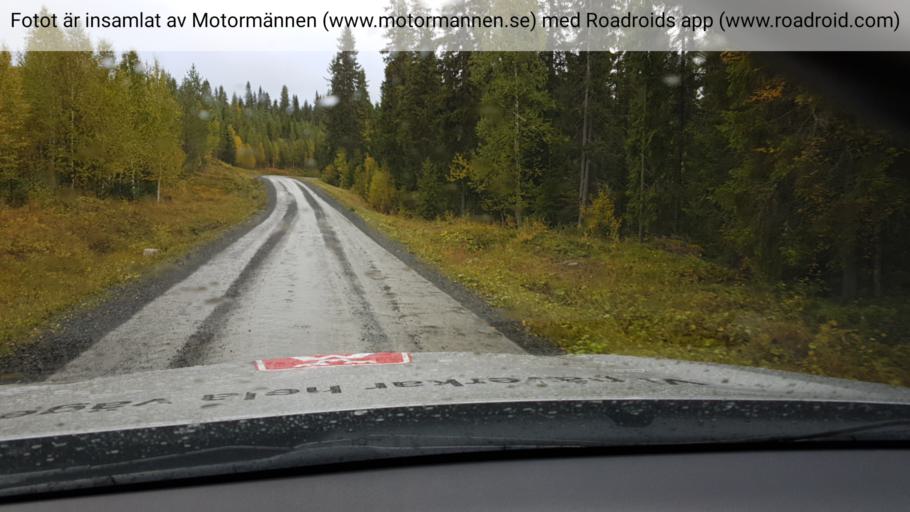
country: SE
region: Jaemtland
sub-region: Krokoms Kommun
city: Valla
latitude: 64.1097
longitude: 14.1478
